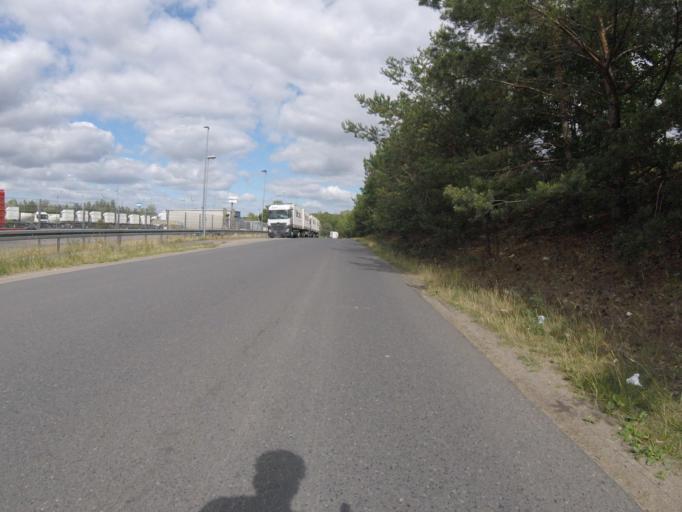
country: DE
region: Brandenburg
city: Wildau
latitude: 52.3142
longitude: 13.6664
